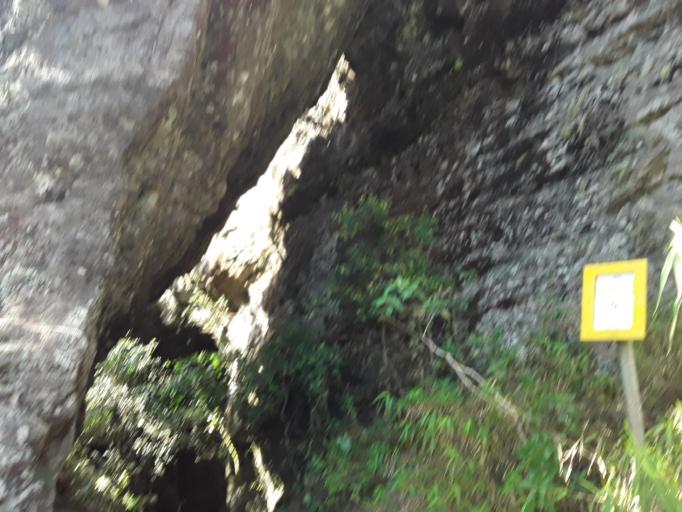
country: BR
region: Minas Gerais
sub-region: Lima Duarte
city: Lima Duarte
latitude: -21.6778
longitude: -43.8833
